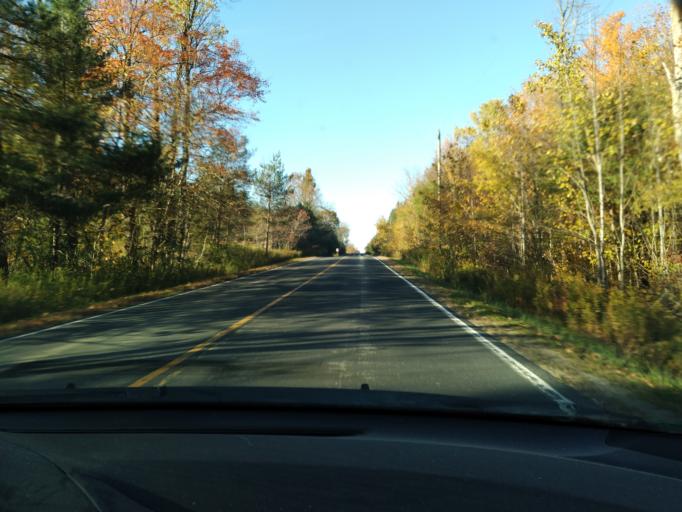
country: CA
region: Ontario
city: Vaughan
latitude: 43.9121
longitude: -79.7060
